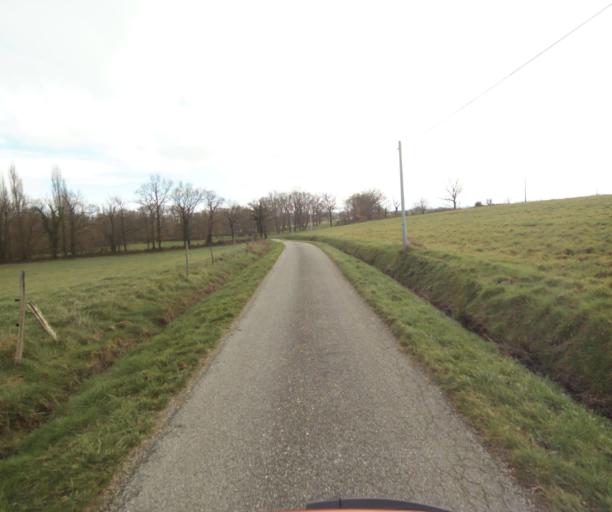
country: FR
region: Languedoc-Roussillon
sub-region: Departement de l'Aude
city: Belpech
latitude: 43.1597
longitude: 1.6993
